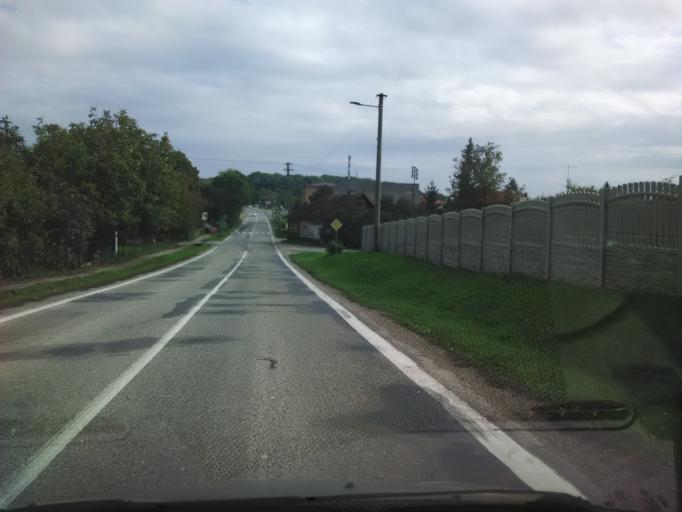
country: SK
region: Nitriansky
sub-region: Okres Nitra
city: Nitra
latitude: 48.2916
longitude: 18.1814
